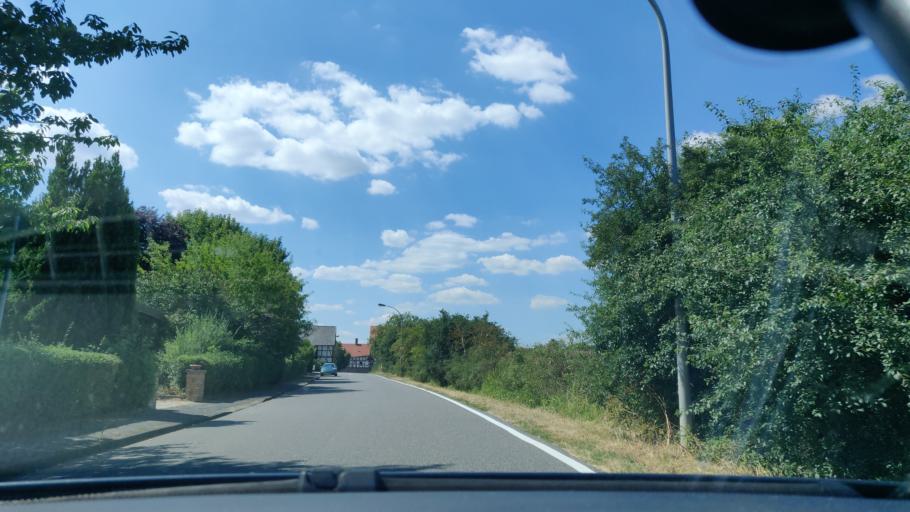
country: DE
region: Hesse
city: Gudensberg
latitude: 51.1505
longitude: 9.3855
